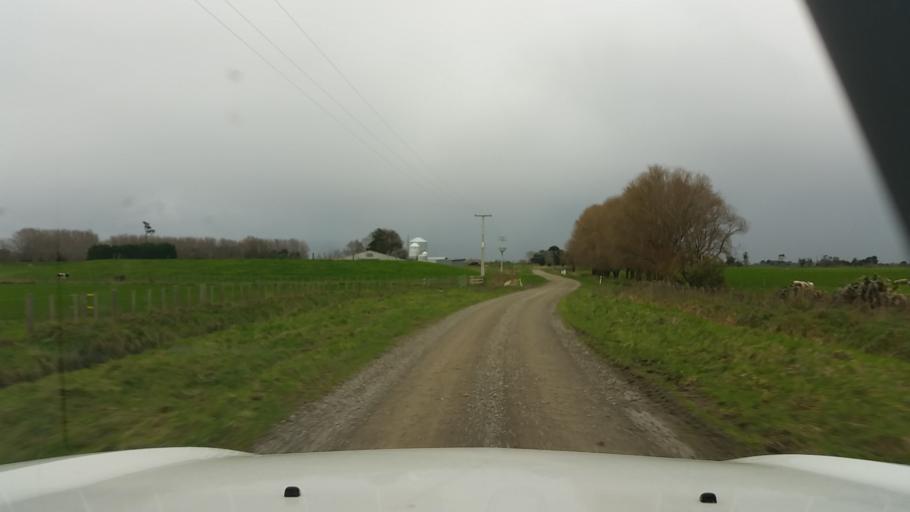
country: NZ
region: Wellington
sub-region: South Wairarapa District
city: Waipawa
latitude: -41.2574
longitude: 175.3706
